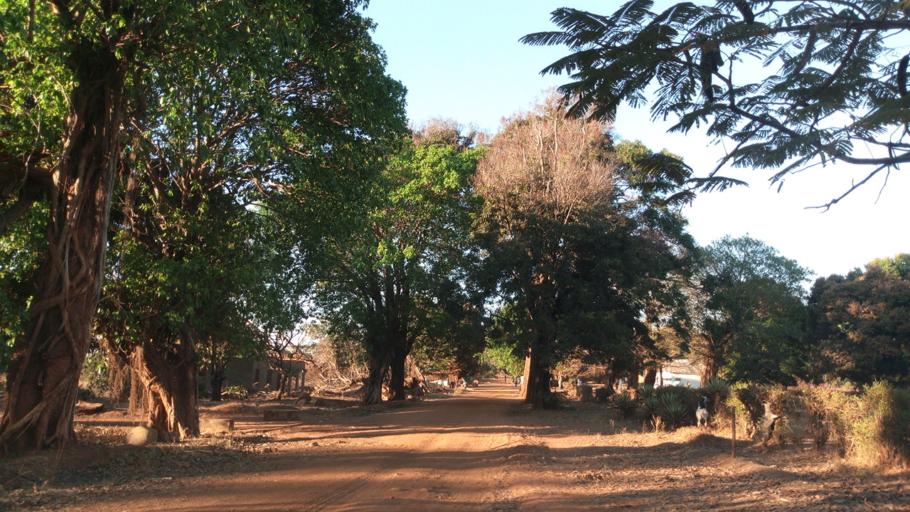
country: ZM
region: Luapula
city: Mwense
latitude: -10.3630
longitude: 28.6153
